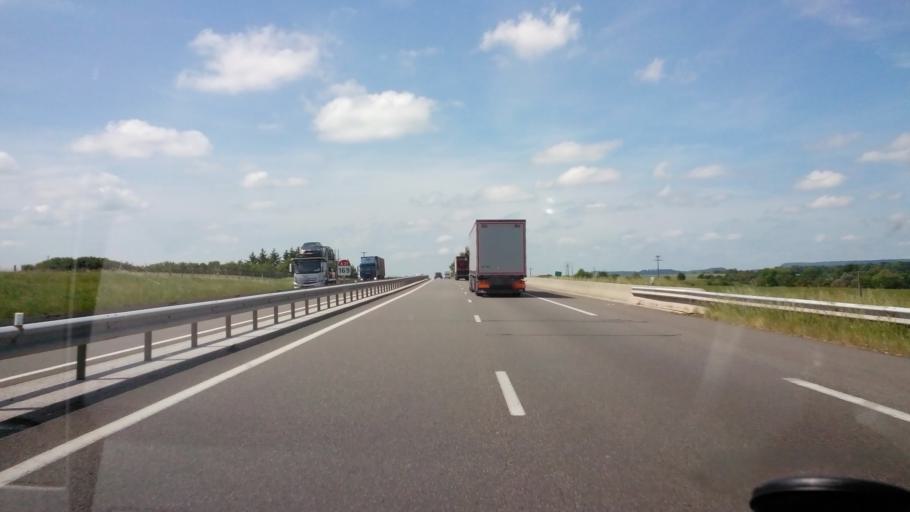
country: FR
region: Lorraine
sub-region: Departement des Vosges
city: Bulgneville
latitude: 48.1872
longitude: 5.7576
